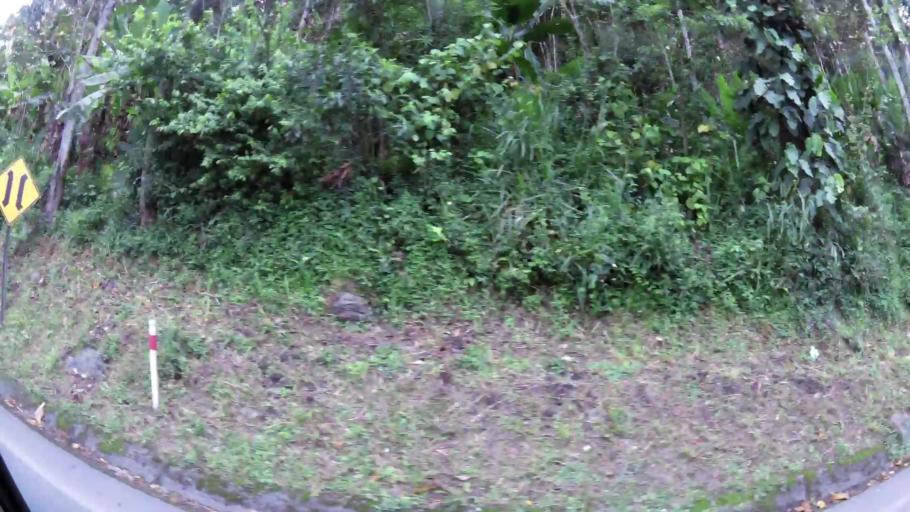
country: EC
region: Santo Domingo de los Tsachilas
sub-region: Canton Santo Domingo de los Colorados
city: Santo Domingo de los Colorados
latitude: -0.2784
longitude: -79.0752
